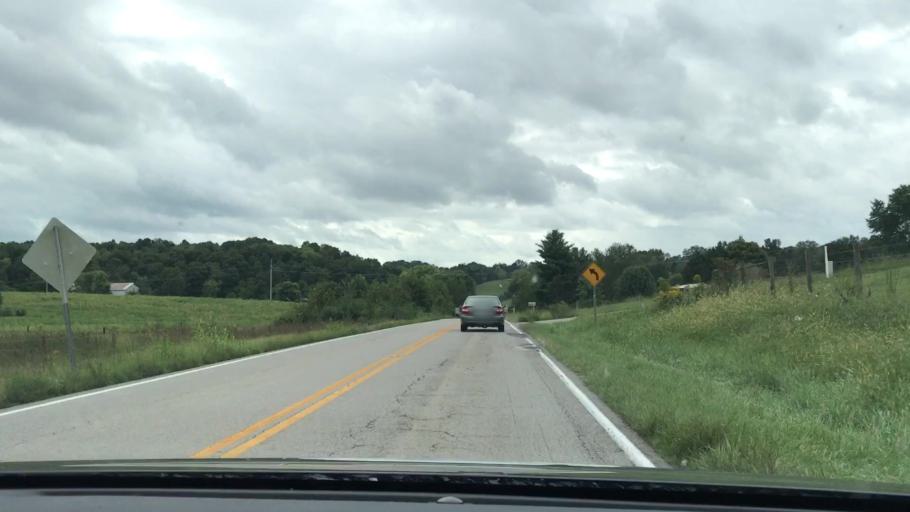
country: US
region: Kentucky
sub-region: Barren County
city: Glasgow
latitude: 36.9162
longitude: -85.7862
